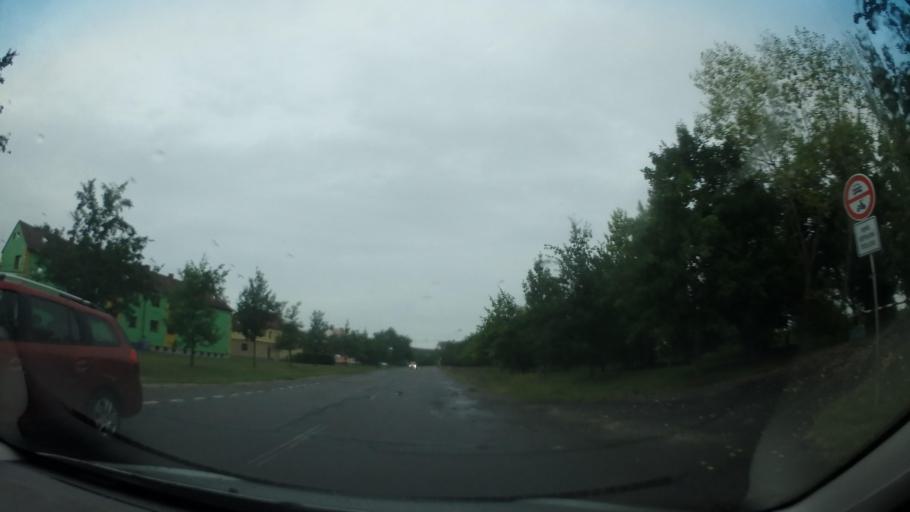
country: CZ
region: Central Bohemia
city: Milovice
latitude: 50.2312
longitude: 14.8896
